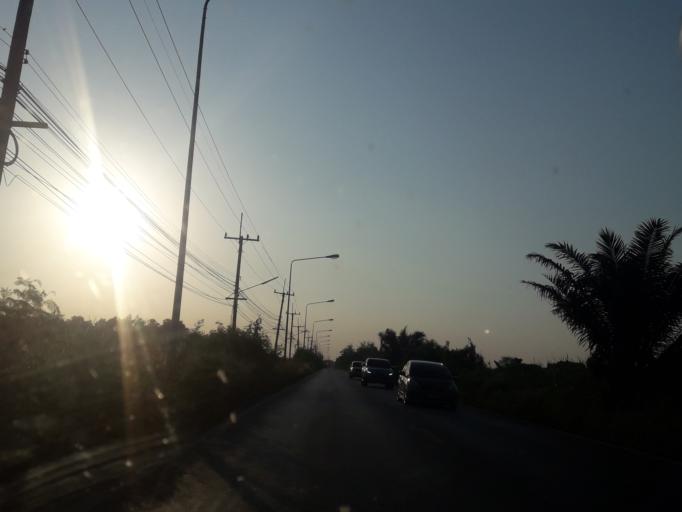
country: TH
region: Pathum Thani
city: Nong Suea
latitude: 14.1315
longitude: 100.7968
